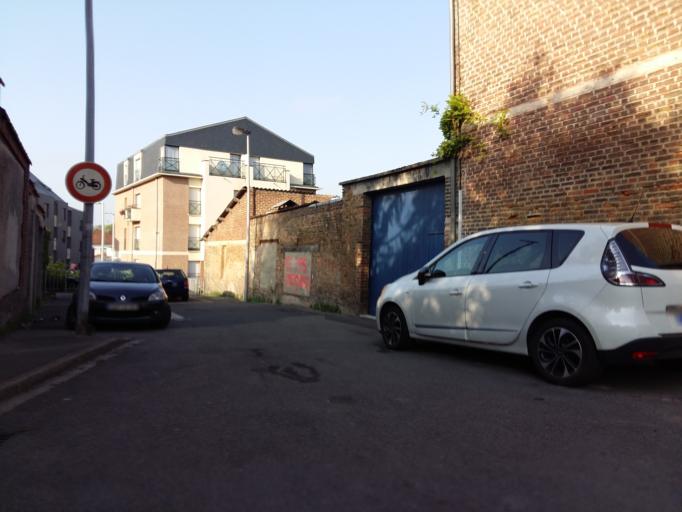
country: FR
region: Picardie
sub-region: Departement de la Somme
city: Amiens
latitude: 49.9031
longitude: 2.2892
